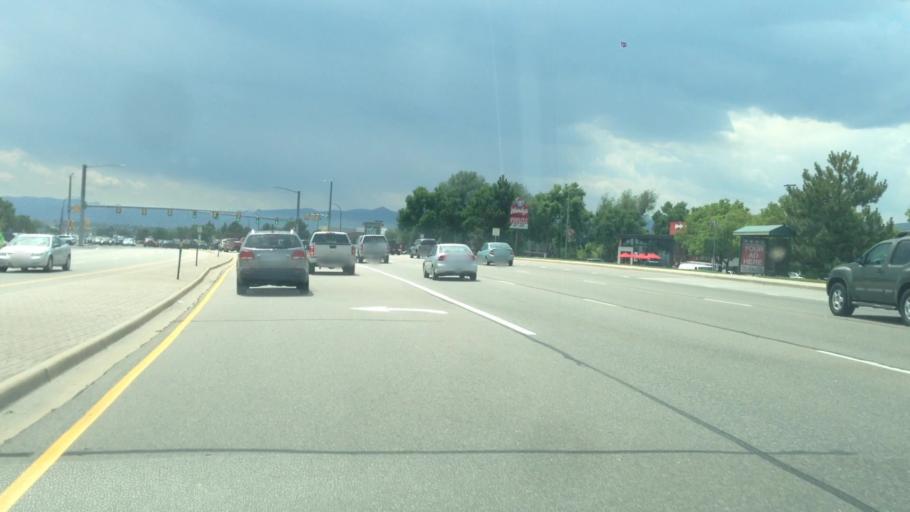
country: US
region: Colorado
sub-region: Jefferson County
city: Columbine
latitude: 39.6257
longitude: -105.0909
